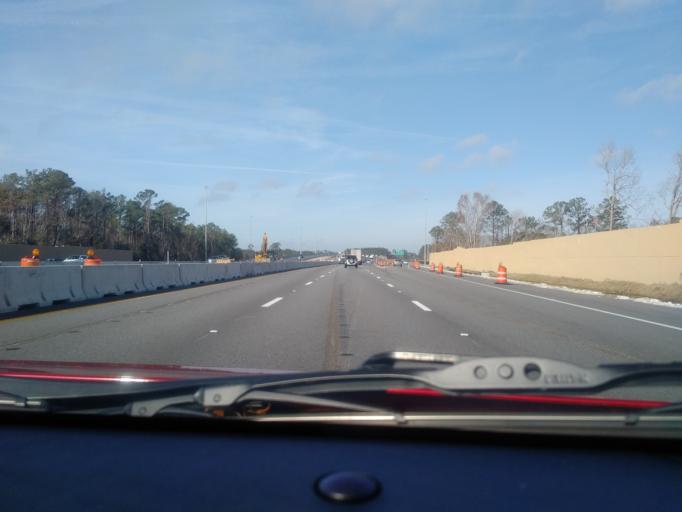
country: US
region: Florida
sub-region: Saint Johns County
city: Fruit Cove
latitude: 30.1689
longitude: -81.5961
